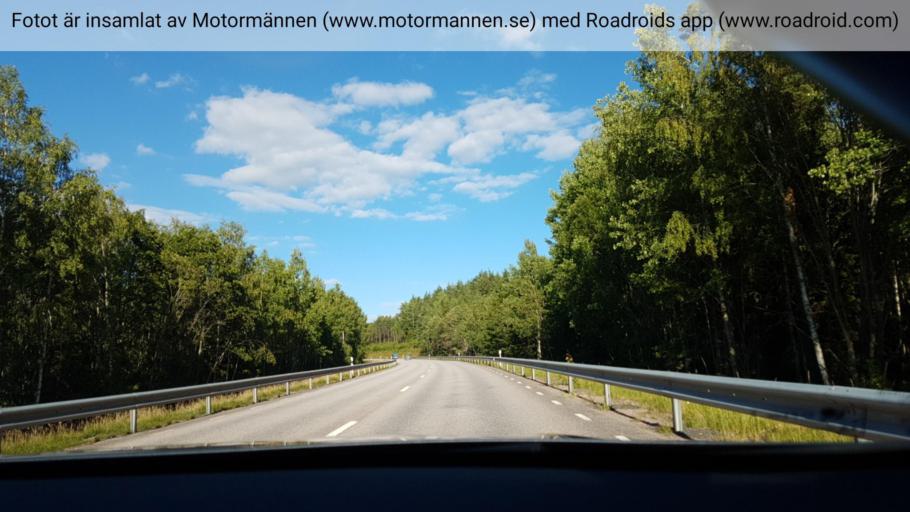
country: SE
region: Vaestra Goetaland
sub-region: Tibro Kommun
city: Tibro
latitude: 58.4536
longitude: 14.2579
